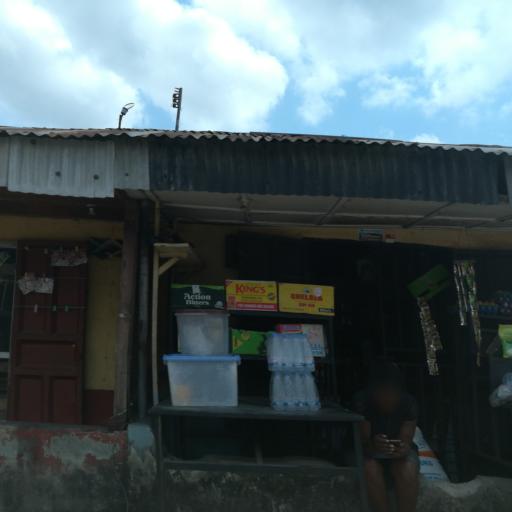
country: NG
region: Rivers
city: Port Harcourt
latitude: 4.7813
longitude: 7.0335
